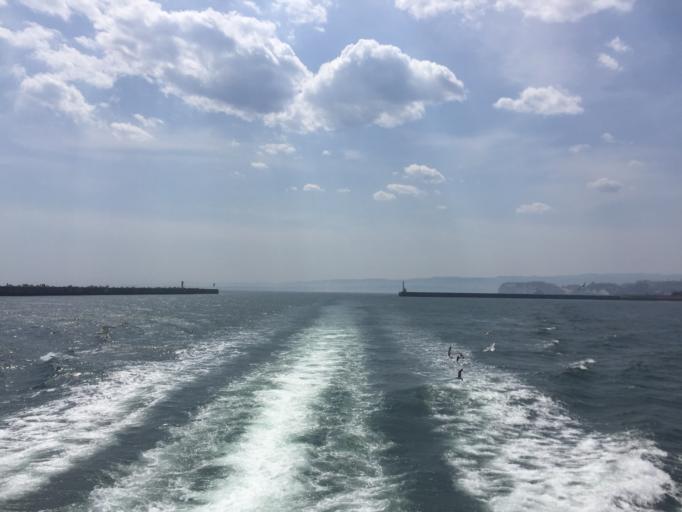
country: JP
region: Fukushima
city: Iwaki
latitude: 36.9195
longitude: 140.8711
